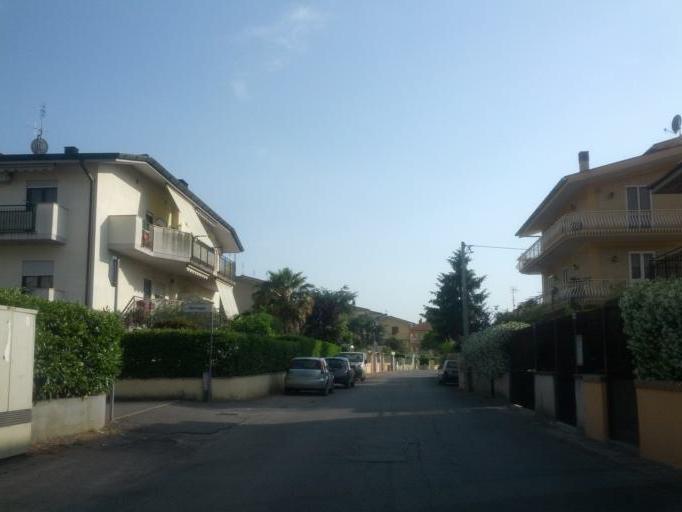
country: IT
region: Latium
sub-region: Provincia di Latina
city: Fondi
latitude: 41.3539
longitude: 13.4197
